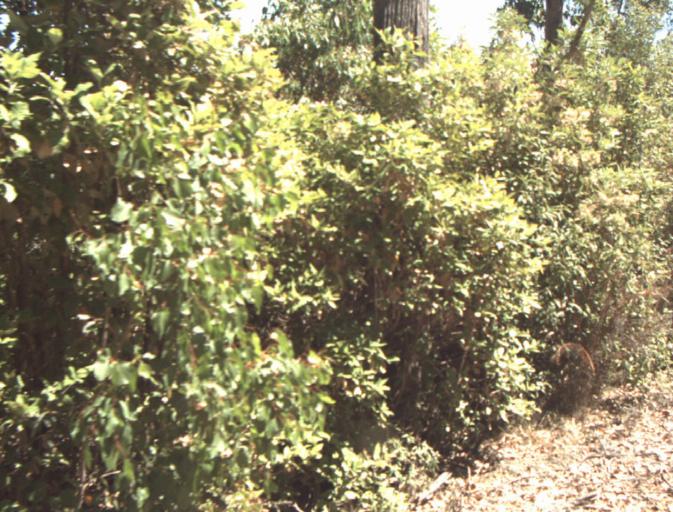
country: AU
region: Tasmania
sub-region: Dorset
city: Scottsdale
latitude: -41.3570
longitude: 147.3927
